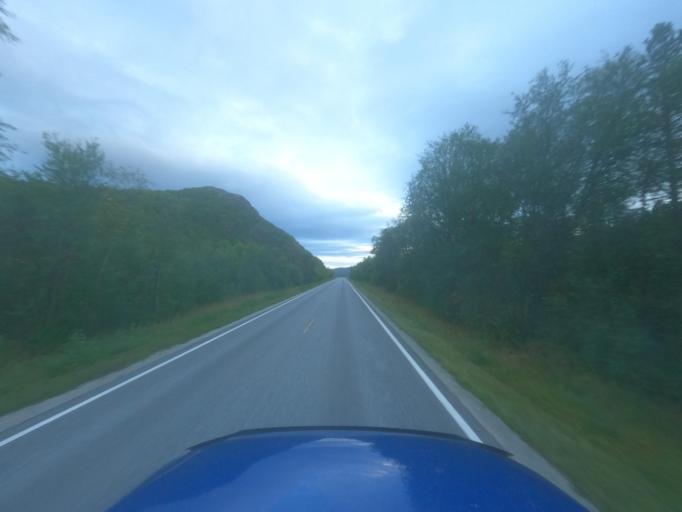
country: NO
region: Finnmark Fylke
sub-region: Porsanger
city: Lakselv
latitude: 69.9219
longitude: 24.9810
